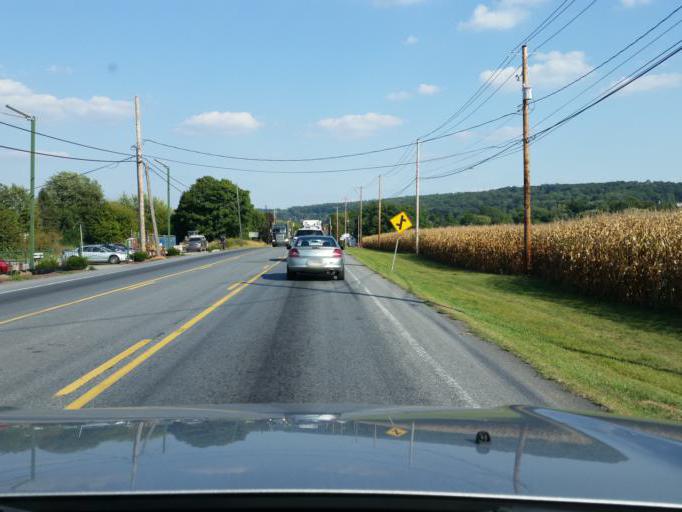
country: US
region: Pennsylvania
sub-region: Lancaster County
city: Gap
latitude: 39.9937
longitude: -76.0318
